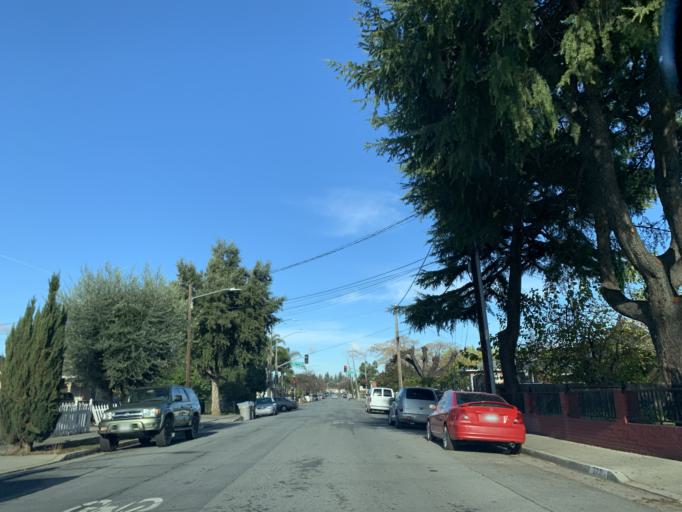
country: US
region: California
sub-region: Santa Clara County
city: Alum Rock
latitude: 37.3519
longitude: -121.8462
